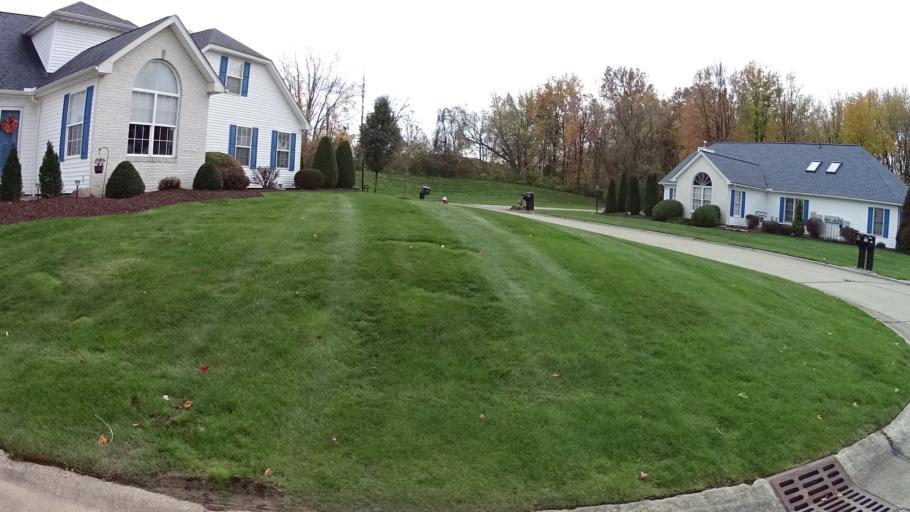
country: US
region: Ohio
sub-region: Lorain County
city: Sheffield Lake
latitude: 41.4816
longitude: -82.1299
